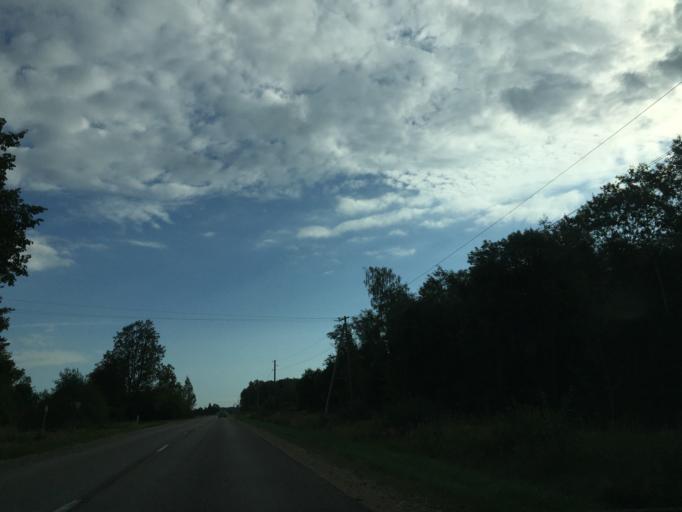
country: LV
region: Saulkrastu
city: Saulkrasti
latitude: 57.5020
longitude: 24.4654
